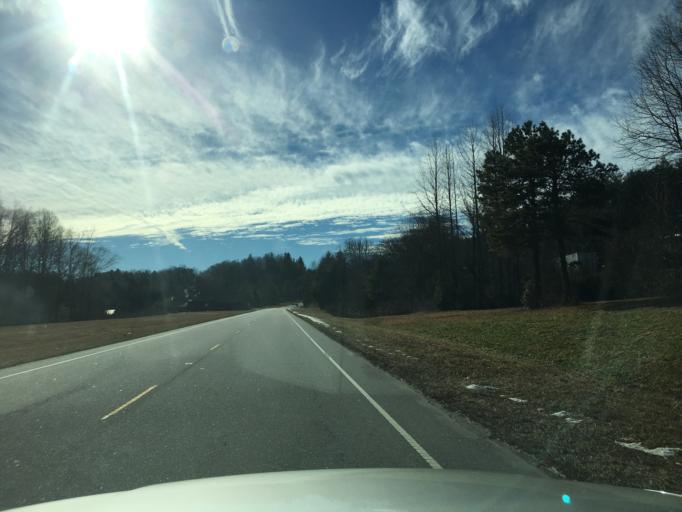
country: US
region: North Carolina
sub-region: Transylvania County
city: Brevard
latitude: 35.1677
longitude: -82.8106
